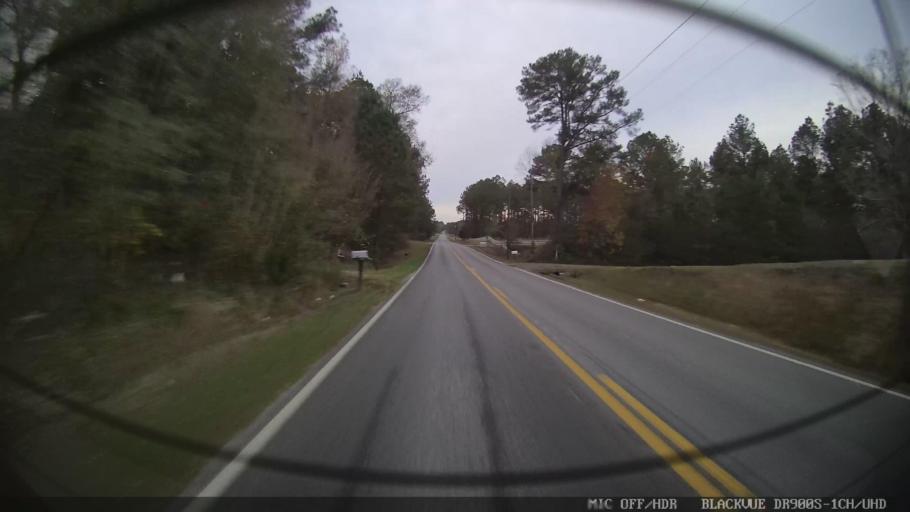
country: US
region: Mississippi
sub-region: Clarke County
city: Quitman
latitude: 32.0291
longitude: -88.7990
